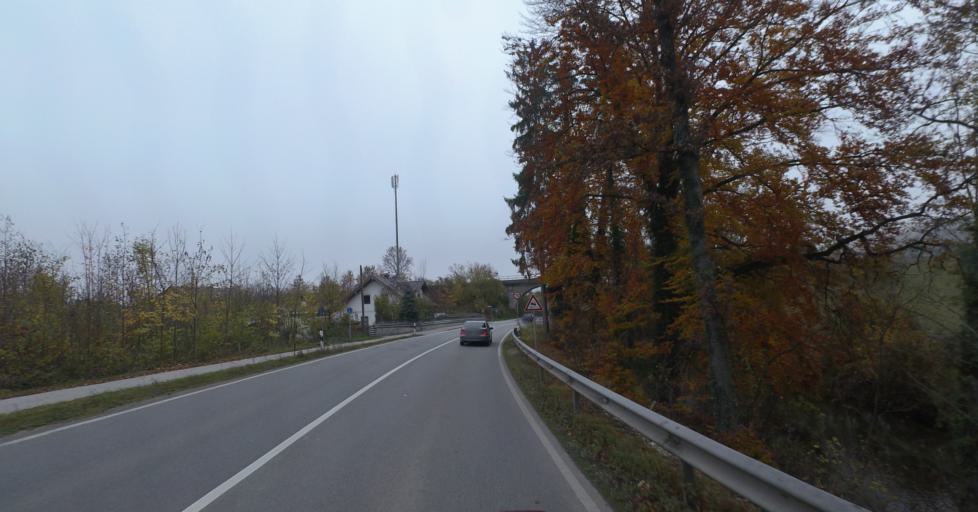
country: DE
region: Bavaria
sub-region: Upper Bavaria
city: Garching an der Alz
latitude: 48.1196
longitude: 12.5735
